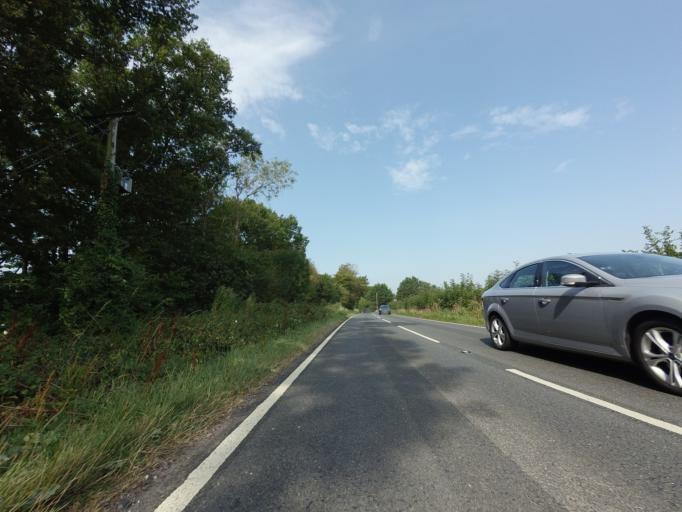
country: GB
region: England
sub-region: Kent
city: Headcorn
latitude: 51.1169
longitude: 0.6165
